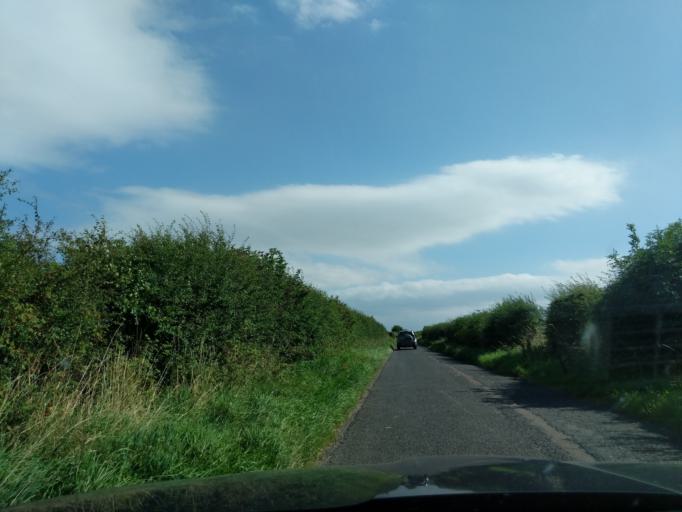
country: GB
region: England
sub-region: Northumberland
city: Ford
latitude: 55.6660
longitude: -2.1631
